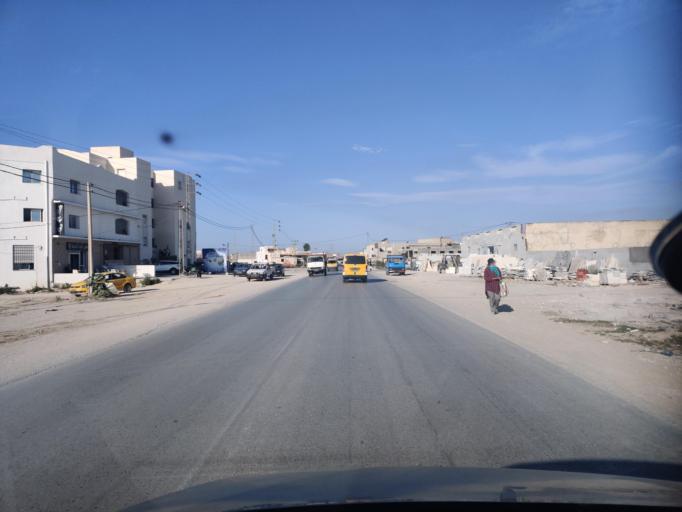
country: TN
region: Ariana
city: Ariana
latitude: 36.9561
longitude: 10.2180
